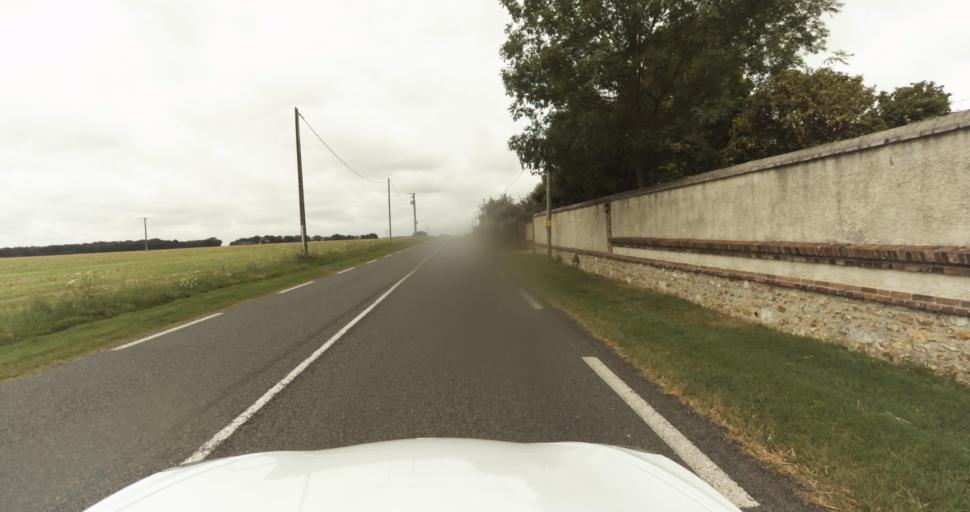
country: FR
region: Haute-Normandie
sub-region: Departement de l'Eure
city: Claville
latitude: 49.0360
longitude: 1.0483
